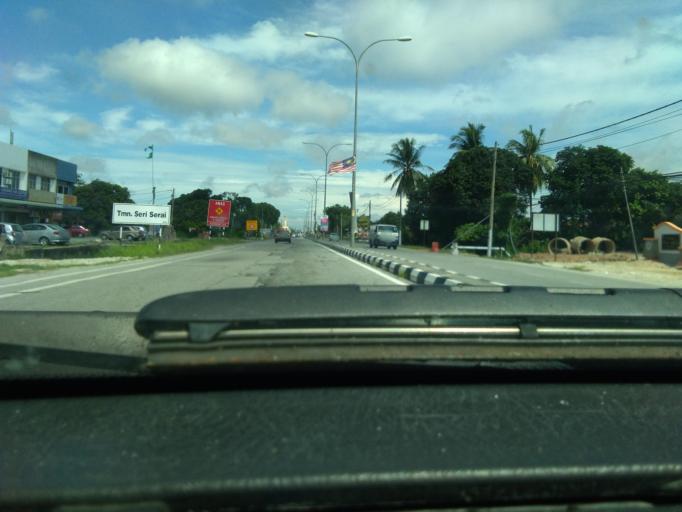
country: MY
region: Perak
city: Bagan Serai
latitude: 5.0067
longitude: 100.5424
